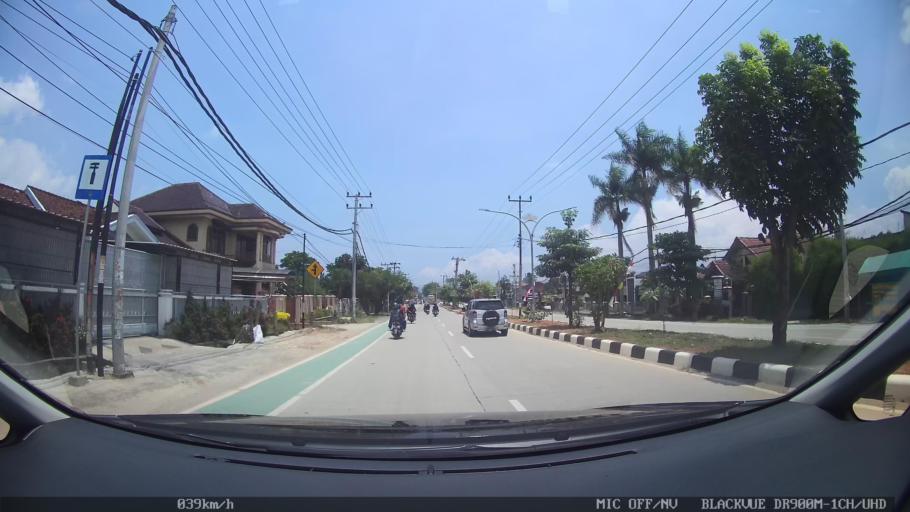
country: ID
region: Lampung
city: Kedaton
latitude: -5.3685
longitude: 105.2998
